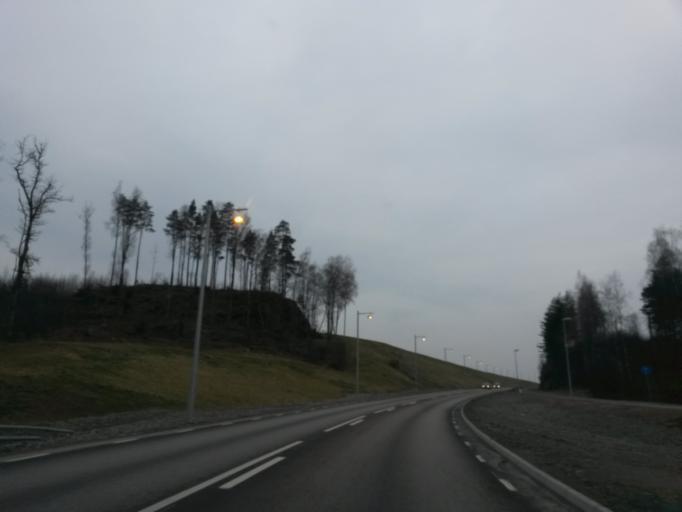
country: SE
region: Vaestra Goetaland
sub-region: Boras Kommun
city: Boras
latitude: 57.7569
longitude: 12.9635
